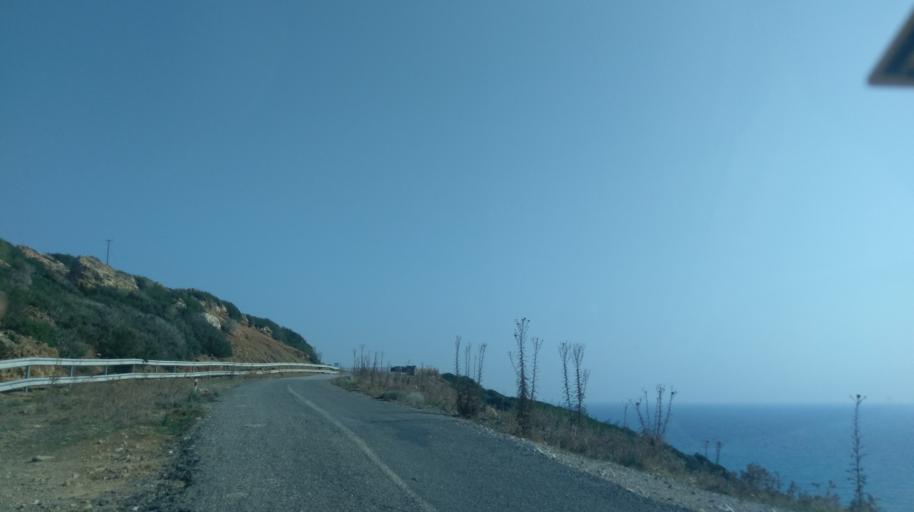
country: CY
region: Ammochostos
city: Rizokarpaso
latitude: 35.6444
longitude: 34.5564
